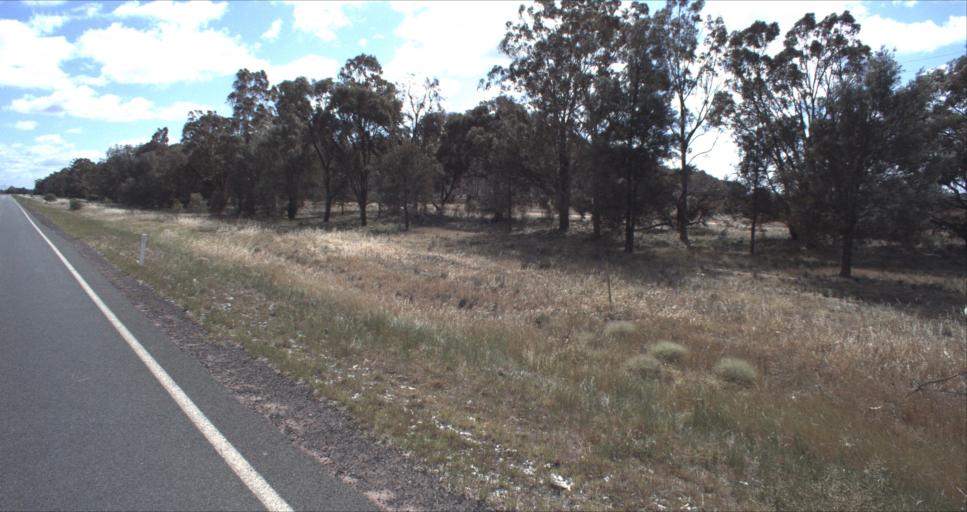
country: AU
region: New South Wales
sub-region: Murrumbidgee Shire
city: Darlington Point
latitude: -34.5877
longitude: 146.1640
